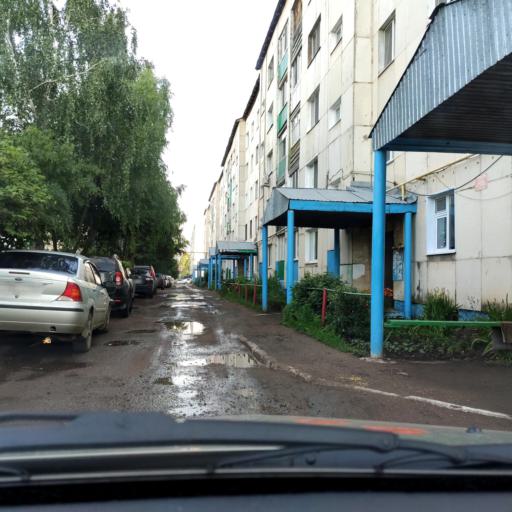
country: RU
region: Bashkortostan
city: Blagoveshchensk
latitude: 55.0306
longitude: 55.9758
